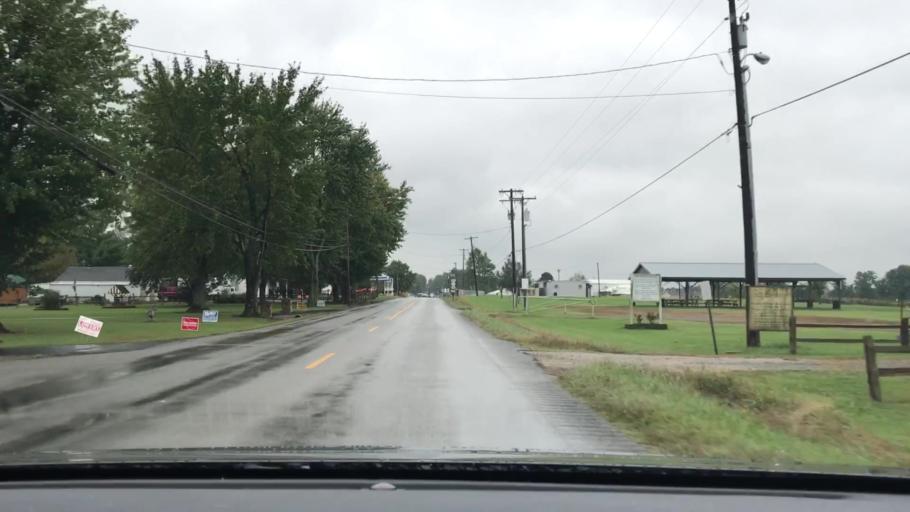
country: US
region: Kentucky
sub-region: McLean County
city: Calhoun
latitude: 37.4085
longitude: -87.2628
